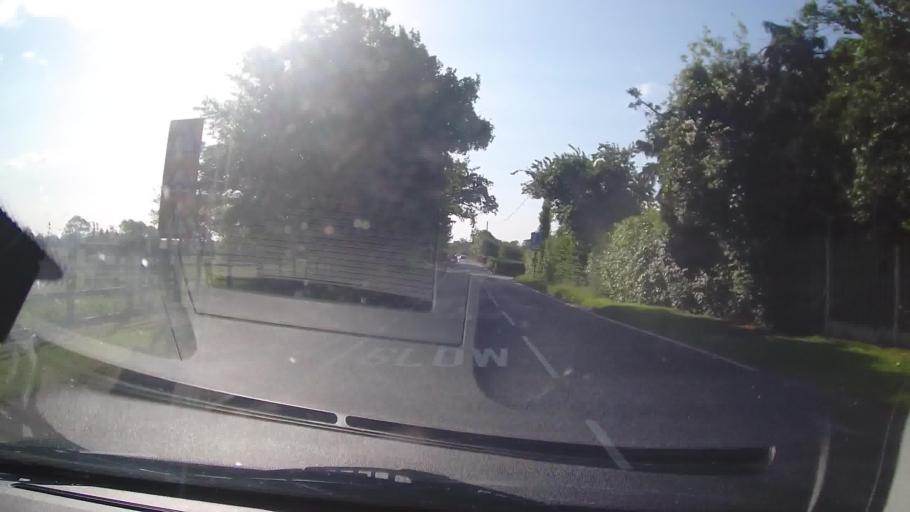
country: GB
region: England
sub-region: Shropshire
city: Withington
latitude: 52.7365
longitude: -2.5711
